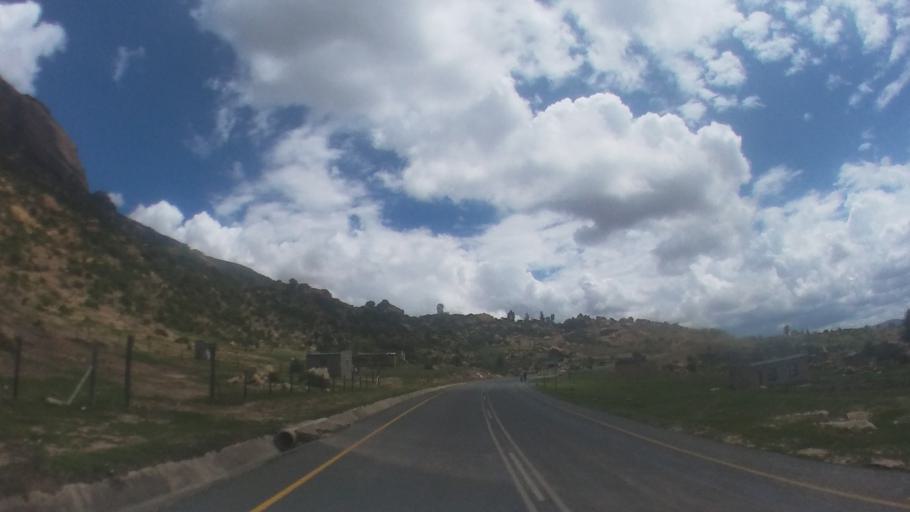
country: LS
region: Maseru
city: Maseru
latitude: -29.4646
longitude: 27.4934
